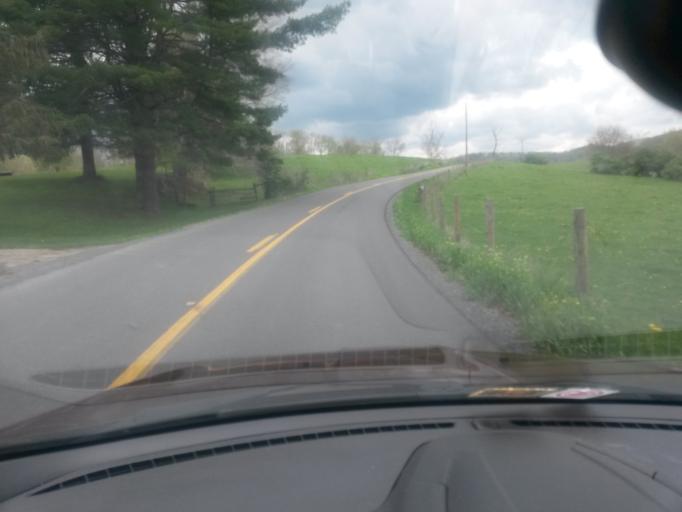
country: US
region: West Virginia
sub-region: Greenbrier County
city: Lewisburg
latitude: 37.9276
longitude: -80.3907
